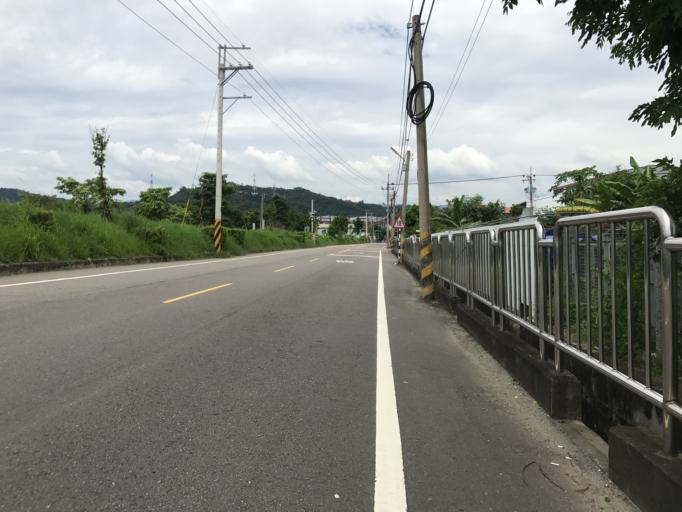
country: TW
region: Taiwan
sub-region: Taichung City
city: Taichung
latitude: 24.0802
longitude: 120.7128
